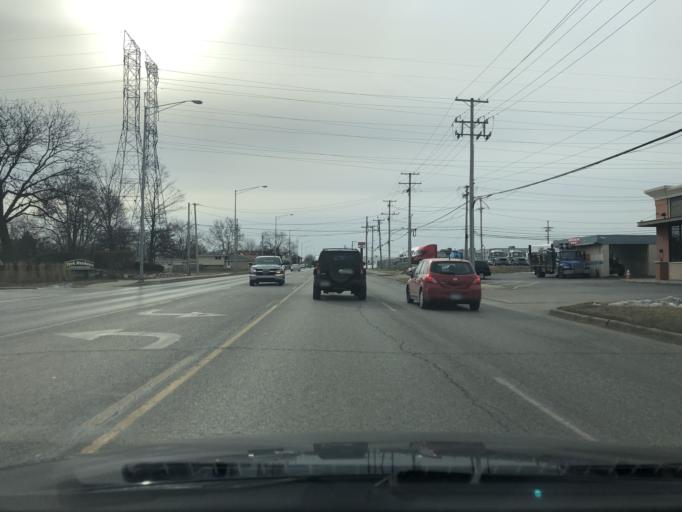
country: US
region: Illinois
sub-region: DuPage County
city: Elmhurst
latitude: 41.9256
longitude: -87.9399
